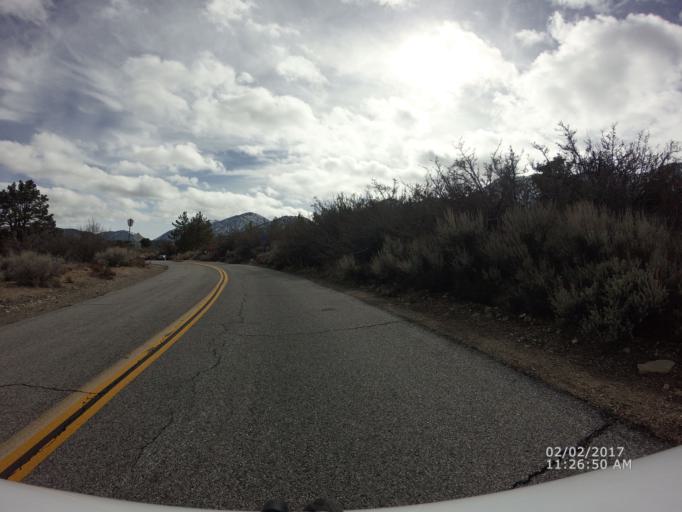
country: US
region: California
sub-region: Los Angeles County
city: Littlerock
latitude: 34.4137
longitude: -117.8598
